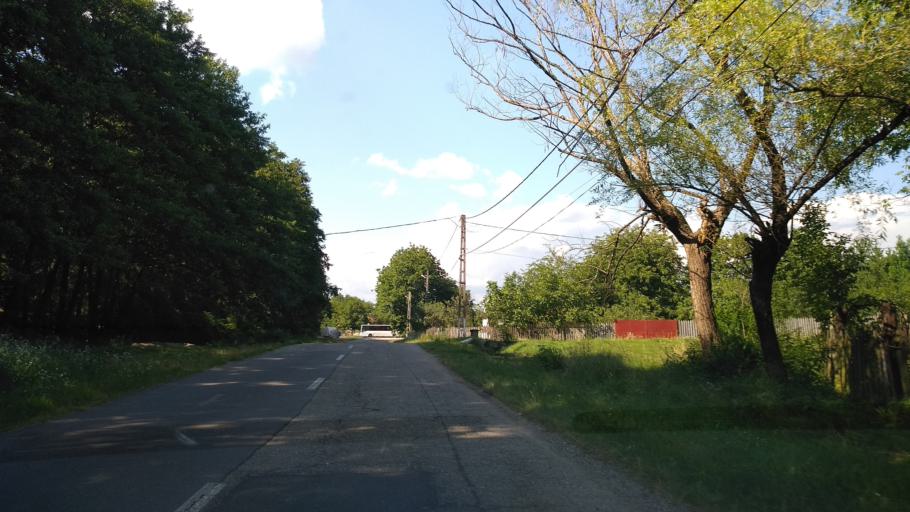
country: RO
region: Hunedoara
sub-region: Comuna Orastioara de Sus
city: Orastioara de Sus
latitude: 45.6933
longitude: 23.1613
